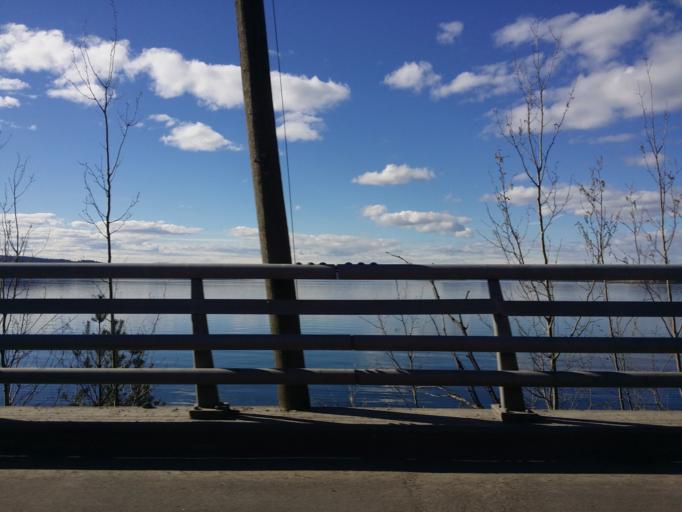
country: NO
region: Akershus
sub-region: Oppegard
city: Kolbotn
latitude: 59.8470
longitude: 10.7770
